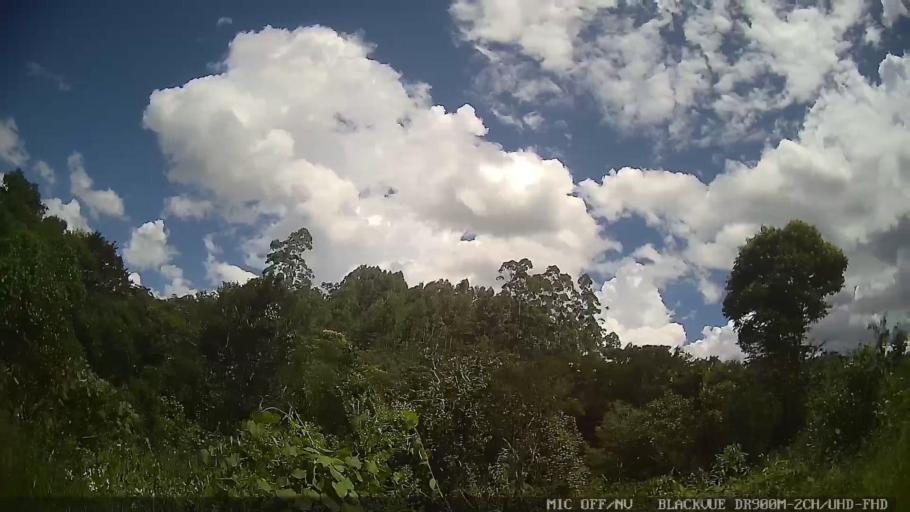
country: BR
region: Sao Paulo
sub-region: Caraguatatuba
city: Caraguatatuba
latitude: -23.5433
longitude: -45.5866
